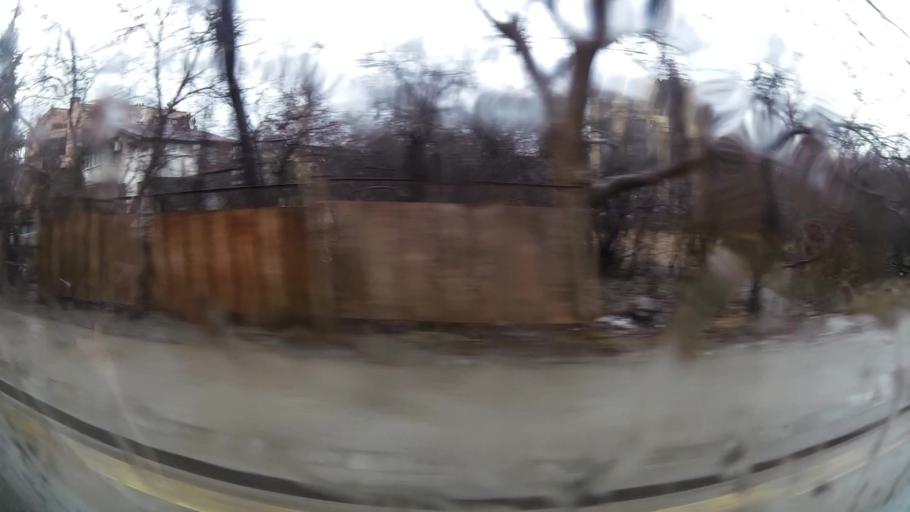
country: BG
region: Sofia-Capital
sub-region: Stolichna Obshtina
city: Sofia
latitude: 42.6548
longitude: 23.3363
